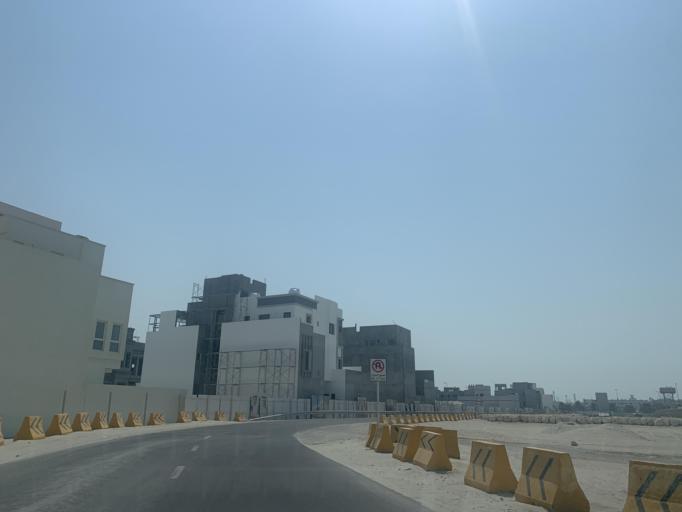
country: BH
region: Muharraq
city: Al Hadd
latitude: 26.2414
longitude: 50.6621
